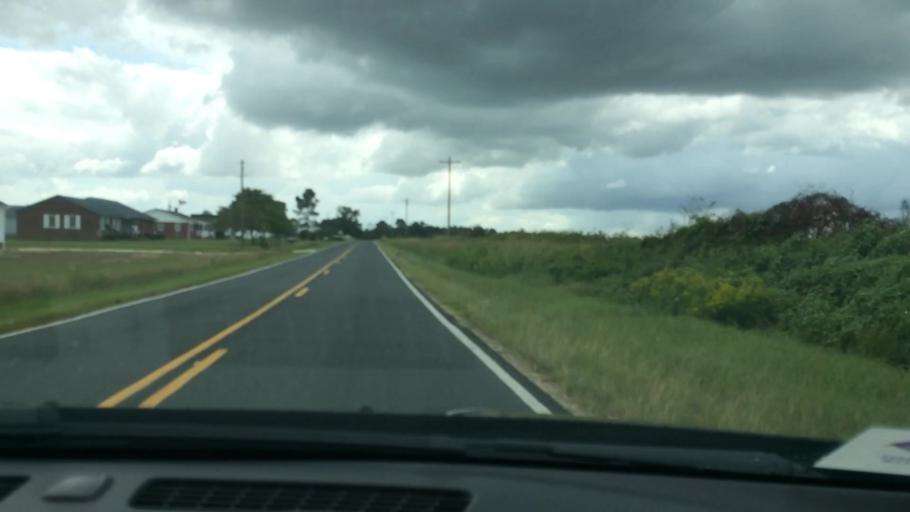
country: US
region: North Carolina
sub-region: Greene County
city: Maury
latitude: 35.5148
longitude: -77.5255
